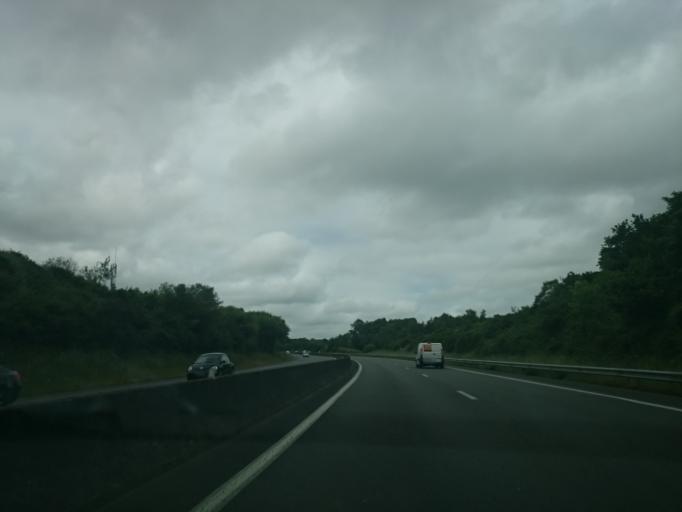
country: FR
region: Pays de la Loire
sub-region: Departement de la Loire-Atlantique
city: Bouaye
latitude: 47.1470
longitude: -1.6994
